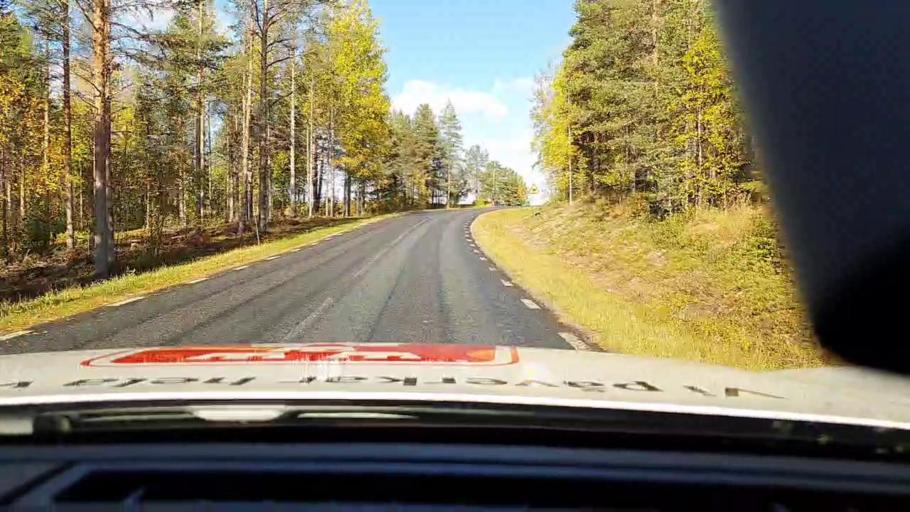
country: SE
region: Vaesterbotten
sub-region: Skelleftea Kommun
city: Langsele
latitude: 65.0028
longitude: 20.0911
